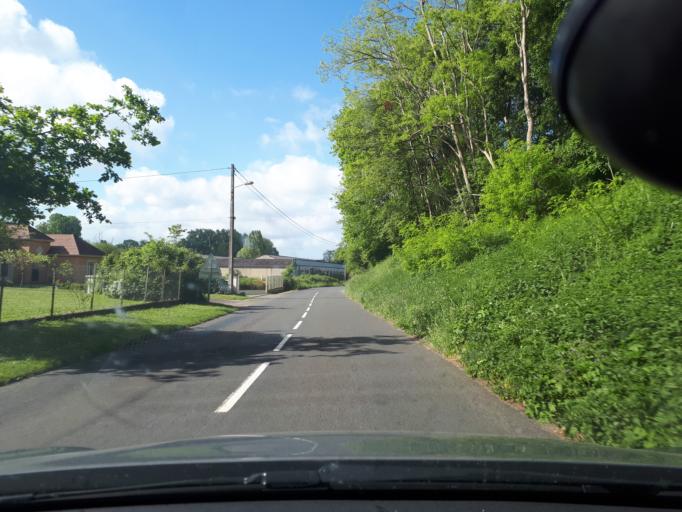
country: FR
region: Pays de la Loire
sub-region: Departement de la Sarthe
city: Change
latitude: 48.0227
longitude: 0.2769
